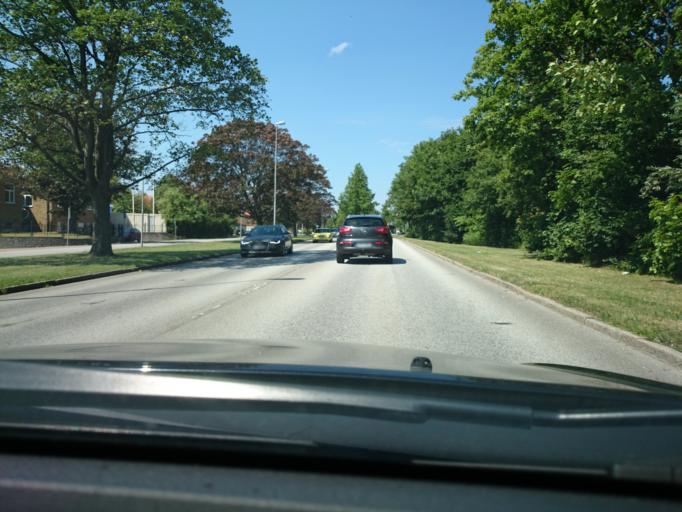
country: SE
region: Skane
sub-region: Landskrona
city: Landskrona
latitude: 55.8849
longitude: 12.8419
